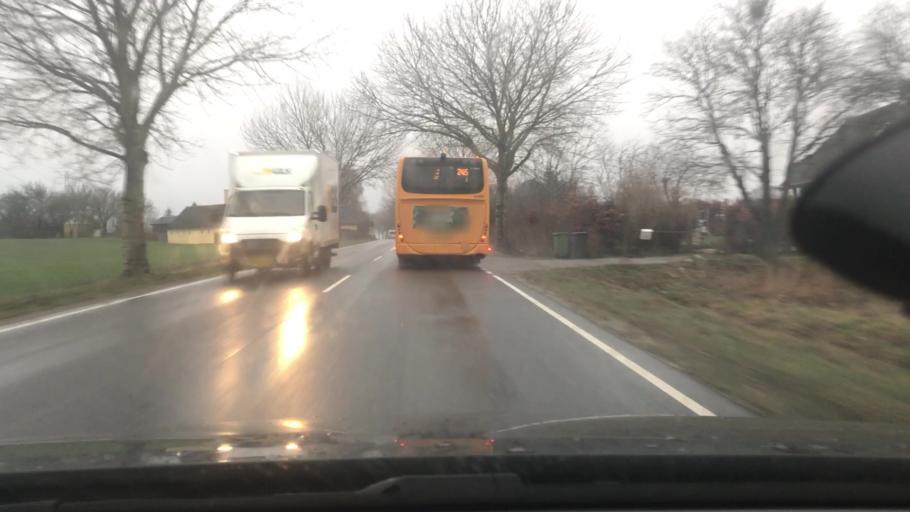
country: DK
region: Zealand
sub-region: Koge Kommune
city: Ejby
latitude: 55.5008
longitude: 12.1053
